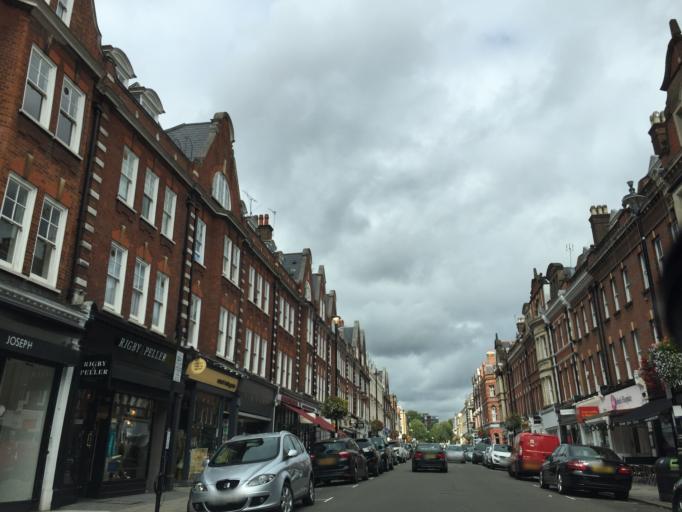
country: GB
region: England
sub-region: Greater London
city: Belsize Park
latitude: 51.5327
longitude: -0.1697
